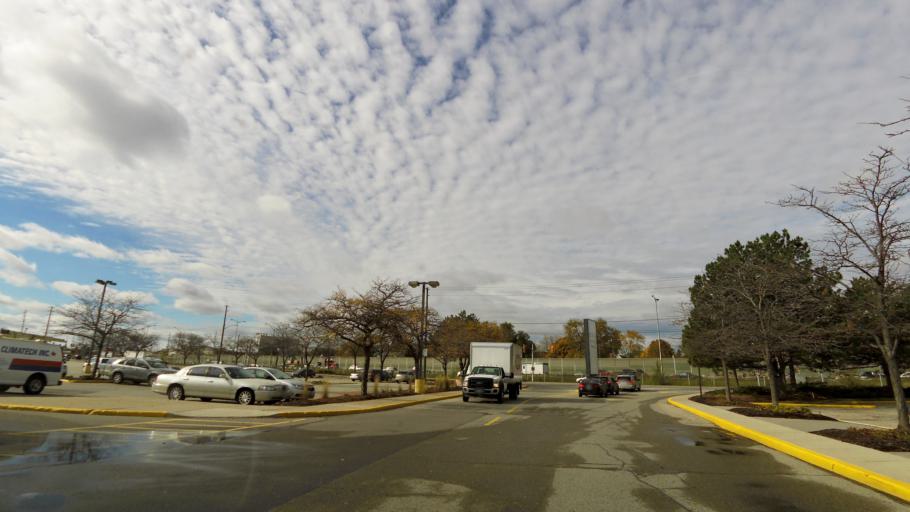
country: CA
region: Ontario
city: Etobicoke
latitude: 43.5937
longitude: -79.5708
